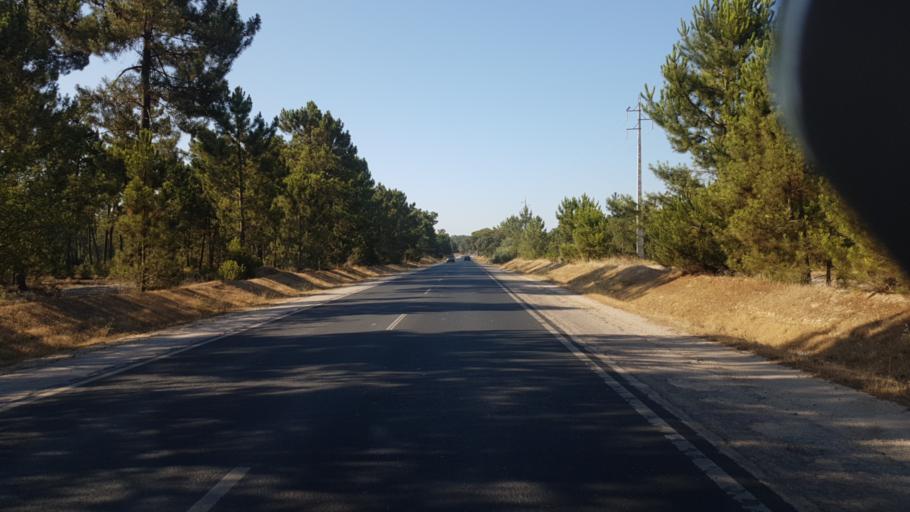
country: PT
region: Setubal
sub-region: Sesimbra
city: Sesimbra
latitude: 38.5299
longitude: -9.1014
